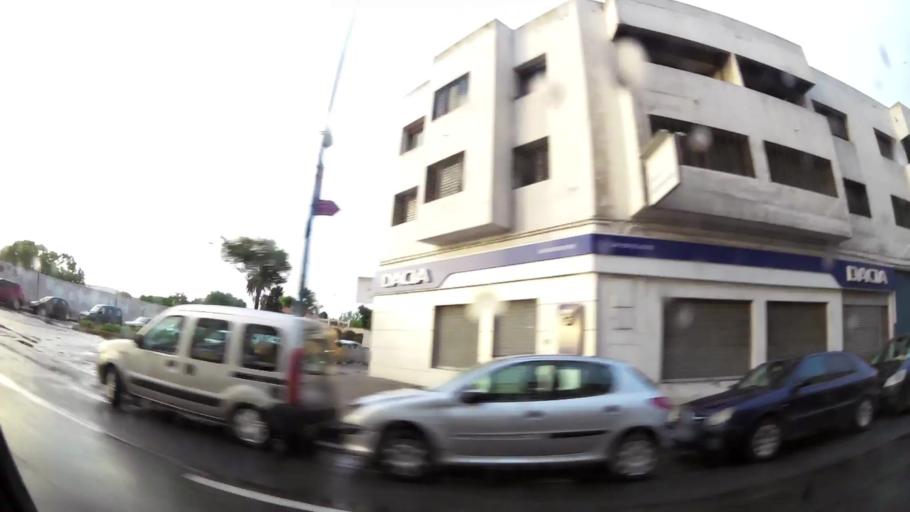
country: MA
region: Grand Casablanca
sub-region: Casablanca
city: Casablanca
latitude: 33.5858
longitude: -7.5823
